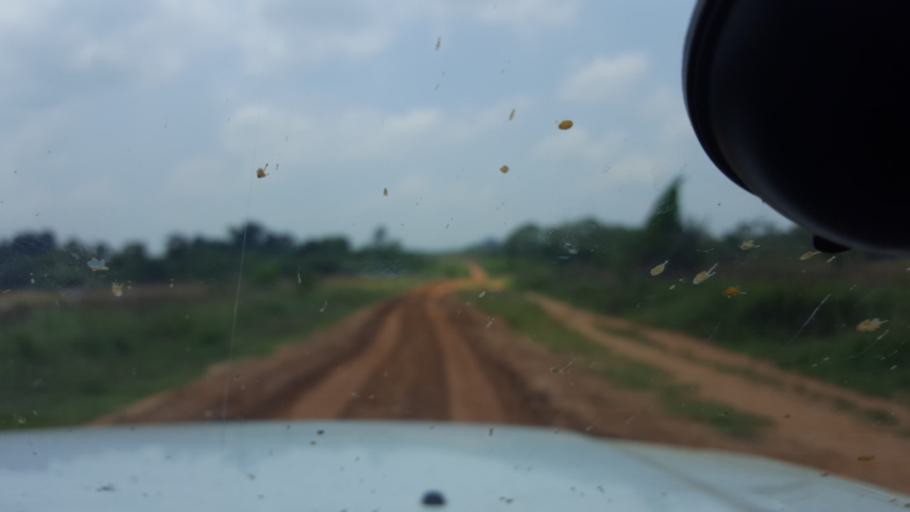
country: CD
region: Bandundu
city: Mushie
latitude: -3.7467
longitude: 16.6571
